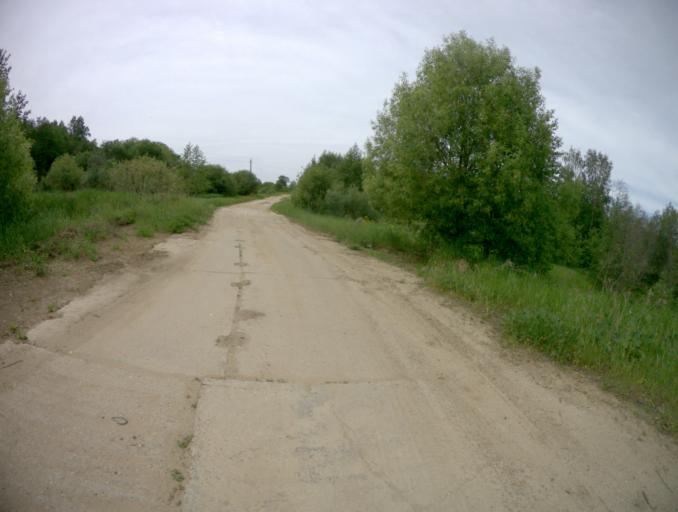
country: RU
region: Vladimir
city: Stavrovo
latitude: 56.1868
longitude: 39.9582
